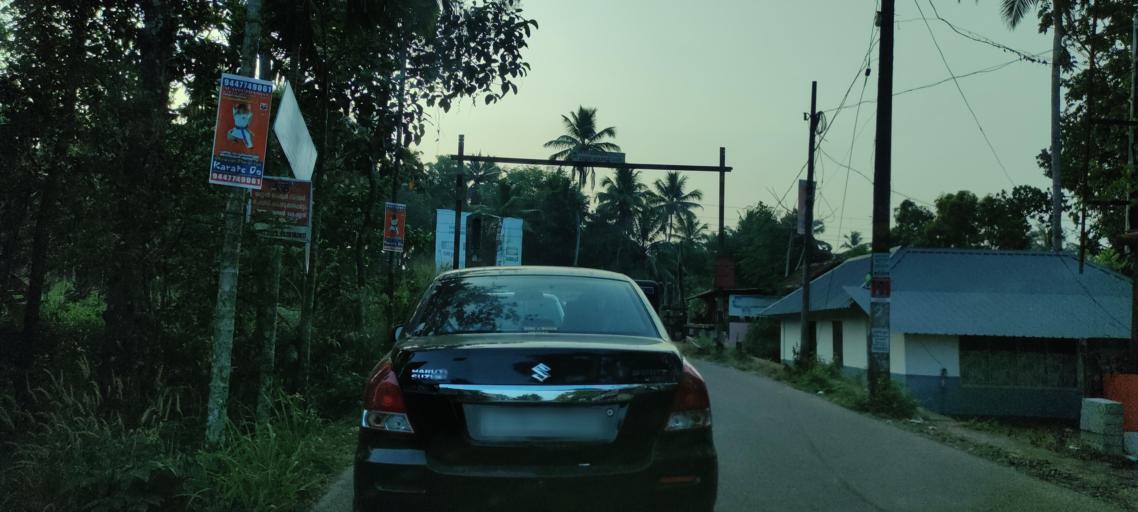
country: IN
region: Kerala
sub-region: Alappuzha
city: Kayankulam
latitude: 9.1361
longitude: 76.5244
